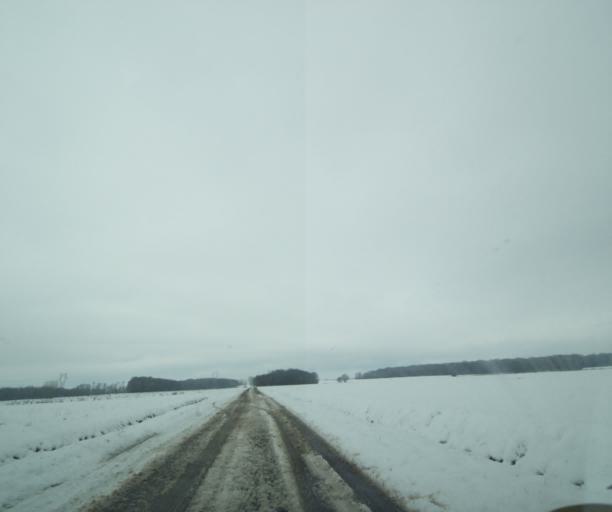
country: FR
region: Champagne-Ardenne
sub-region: Departement de la Haute-Marne
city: Montier-en-Der
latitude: 48.5124
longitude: 4.7594
